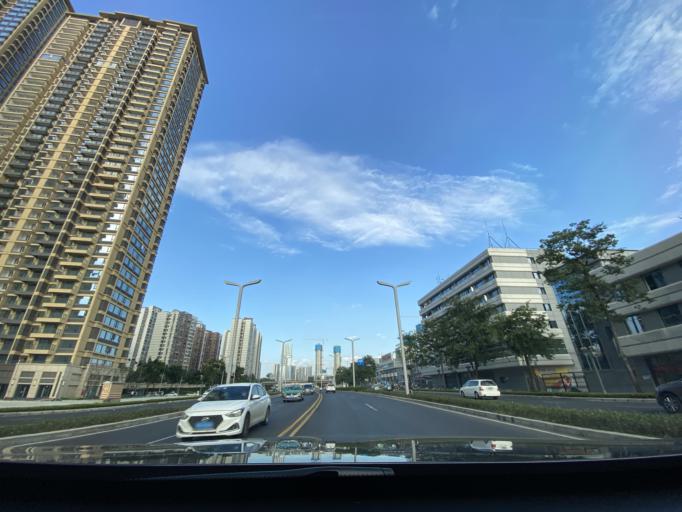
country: CN
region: Sichuan
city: Chengdu
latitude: 30.6387
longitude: 104.1238
